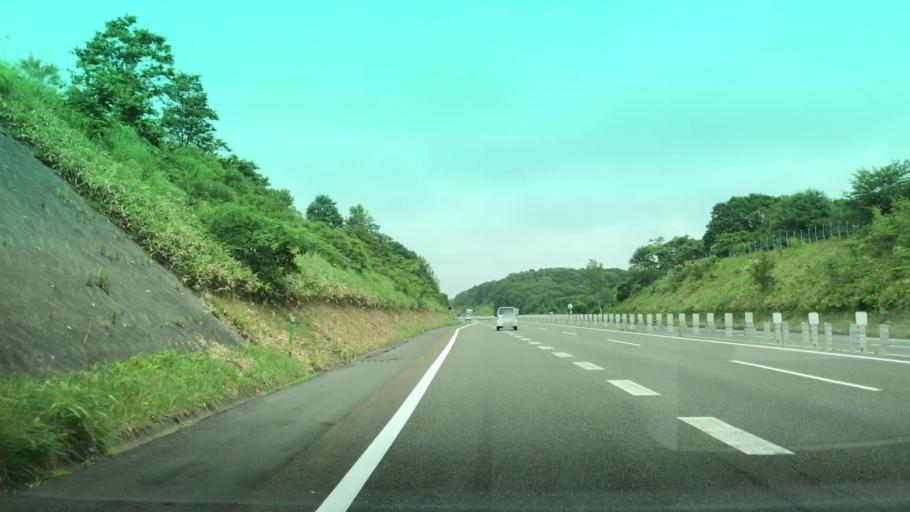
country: JP
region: Hokkaido
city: Tomakomai
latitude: 42.6168
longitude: 141.4720
